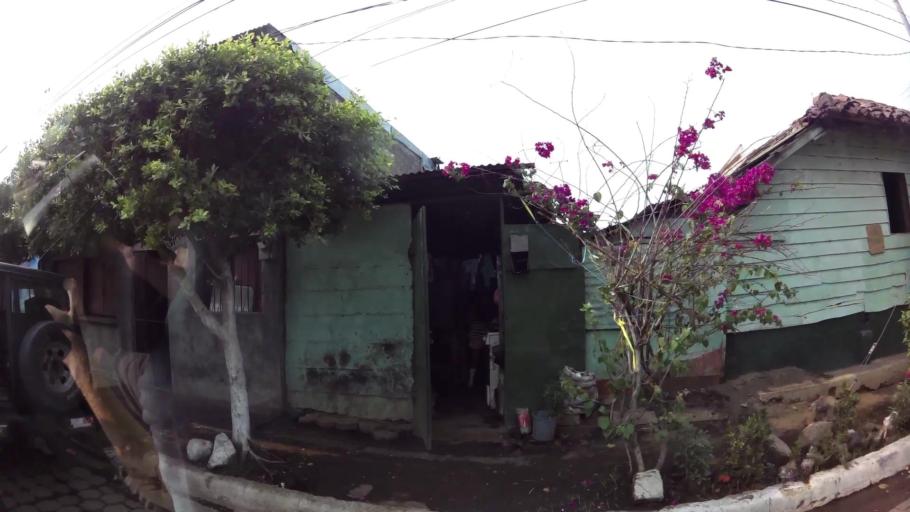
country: NI
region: Chinandega
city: Chinandega
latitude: 12.6247
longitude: -87.1297
